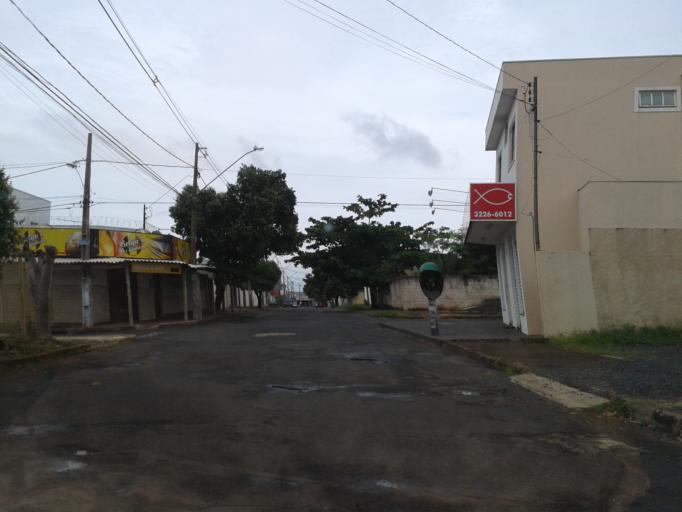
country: BR
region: Minas Gerais
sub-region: Uberlandia
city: Uberlandia
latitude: -18.9319
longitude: -48.2471
